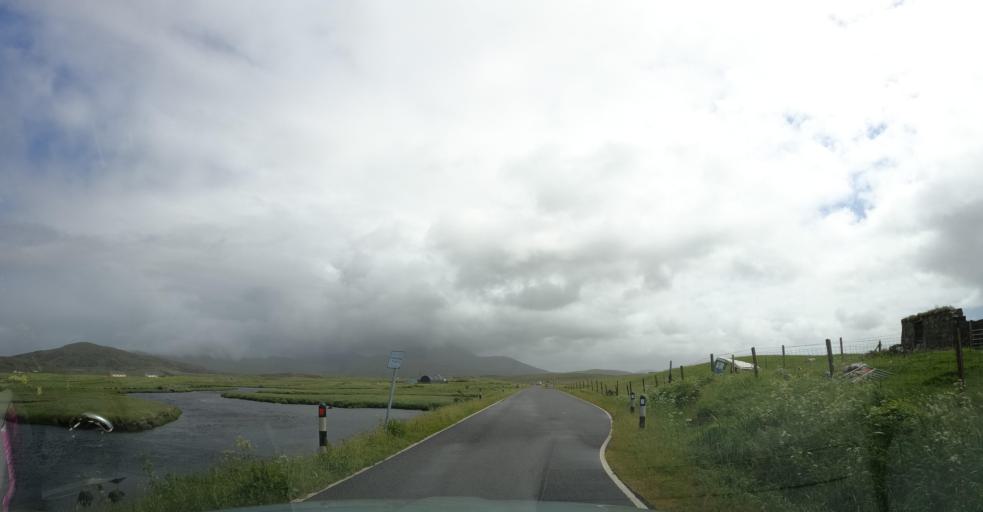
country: GB
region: Scotland
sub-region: Eilean Siar
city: Isle of South Uist
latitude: 57.2959
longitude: -7.3875
